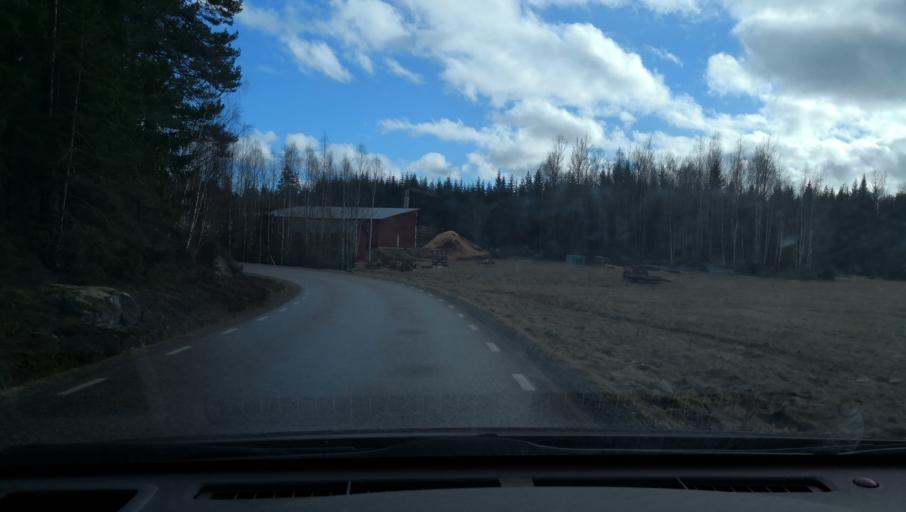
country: SE
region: Vaestmanland
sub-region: Arboga Kommun
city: Arboga
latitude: 59.3383
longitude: 15.7032
